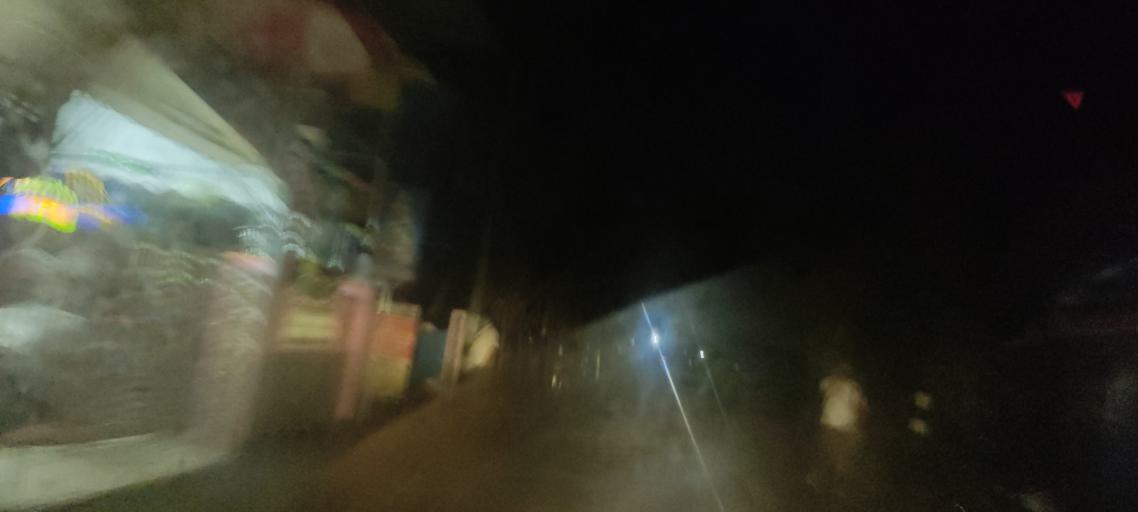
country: IN
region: Kerala
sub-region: Alappuzha
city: Vayalar
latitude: 9.7209
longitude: 76.3374
